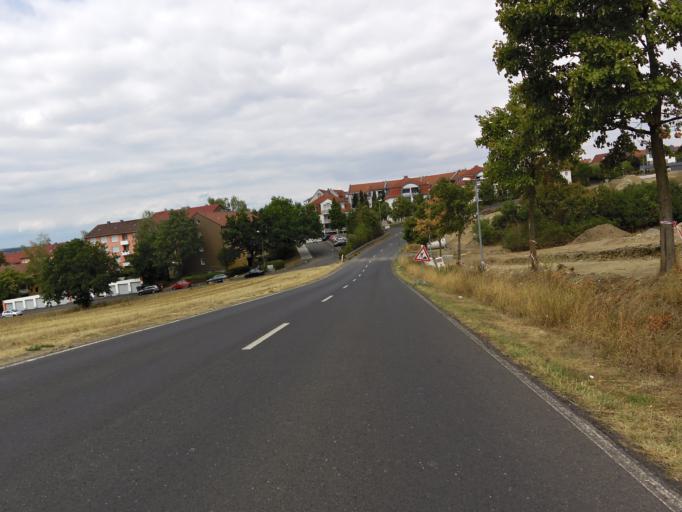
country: DE
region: Bavaria
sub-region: Regierungsbezirk Unterfranken
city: Veitshochheim
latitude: 49.8291
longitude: 9.8898
